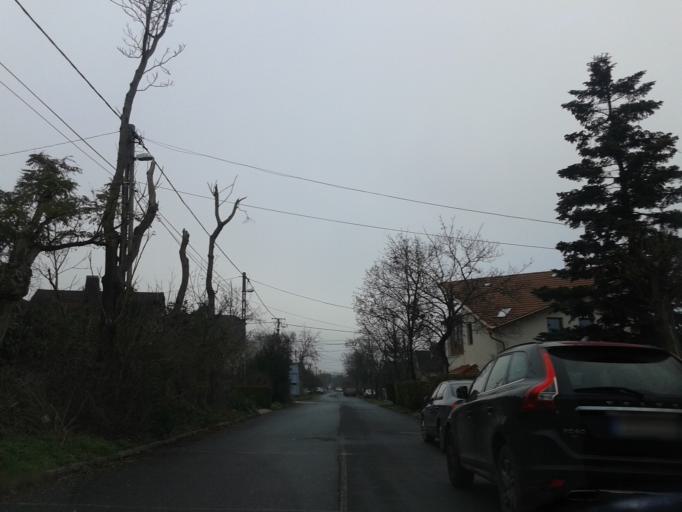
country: HU
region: Budapest
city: Budapest XXII. keruelet
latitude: 47.4241
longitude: 19.0130
